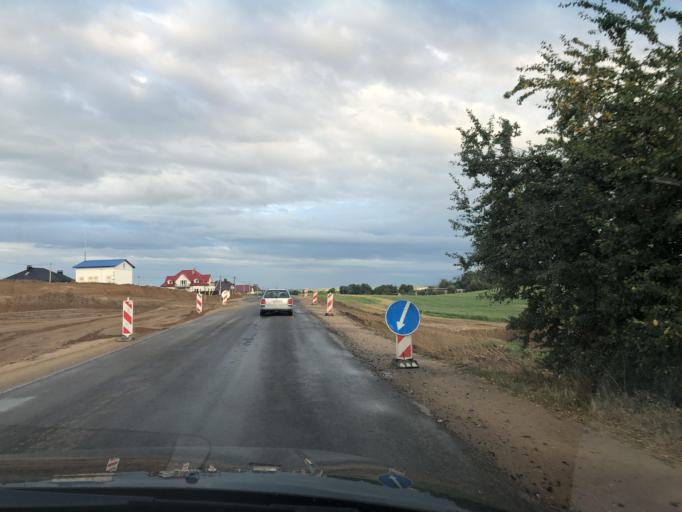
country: BY
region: Grodnenskaya
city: Hrodna
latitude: 53.7114
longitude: 23.8850
